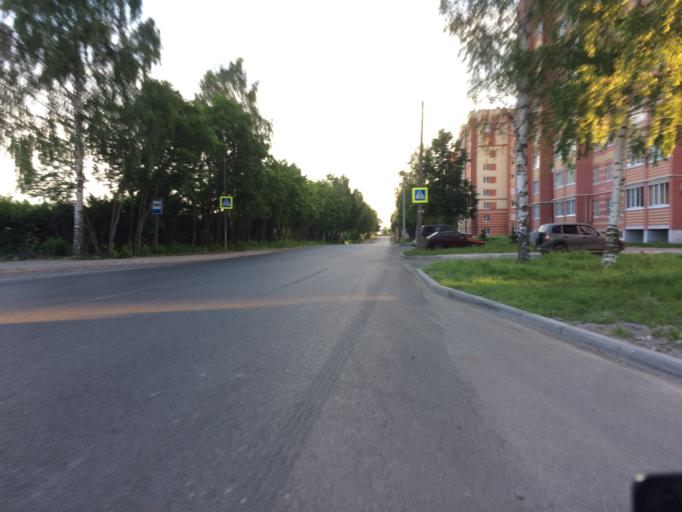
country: RU
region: Mariy-El
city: Medvedevo
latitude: 56.6449
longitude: 47.8313
